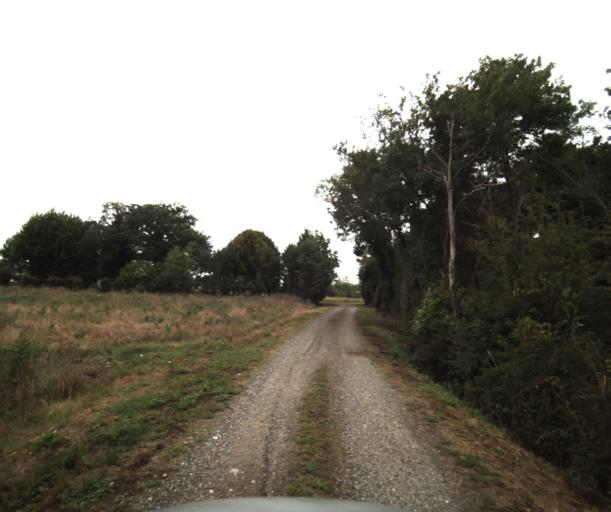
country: FR
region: Midi-Pyrenees
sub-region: Departement de la Haute-Garonne
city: Seysses
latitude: 43.4501
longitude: 1.3045
